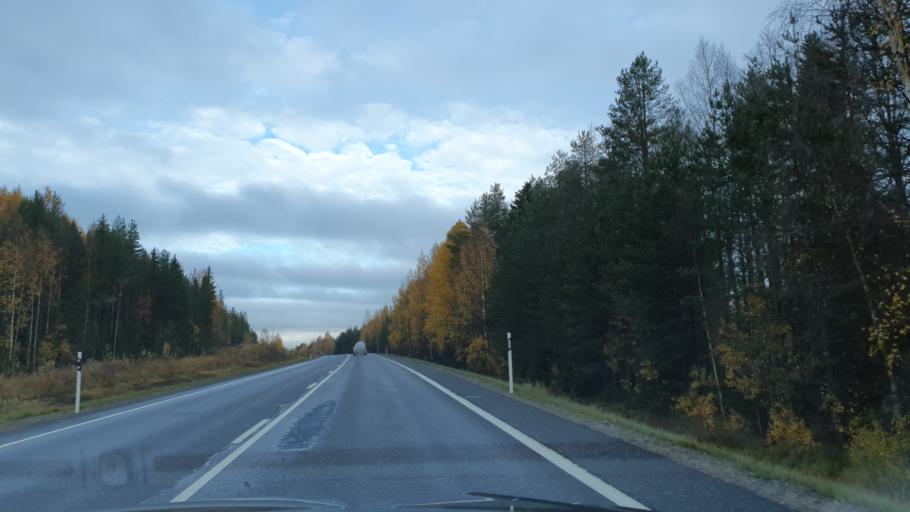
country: FI
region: Lapland
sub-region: Rovaniemi
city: Rovaniemi
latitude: 66.5879
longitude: 25.6130
